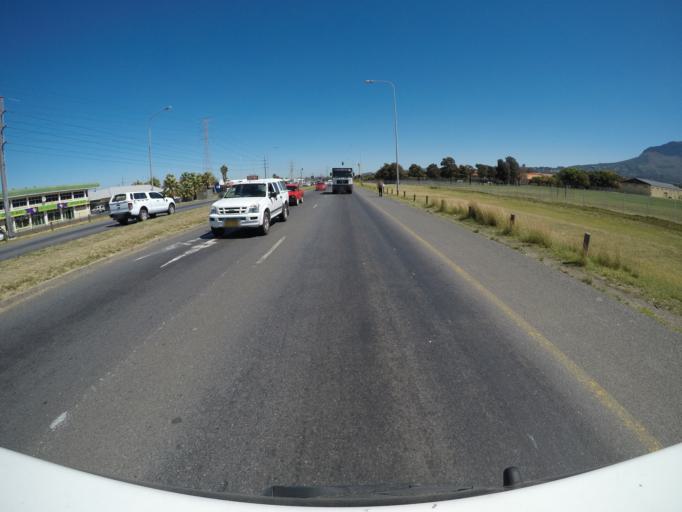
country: ZA
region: Western Cape
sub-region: Cape Winelands District Municipality
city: Stellenbosch
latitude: -34.0953
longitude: 18.8459
